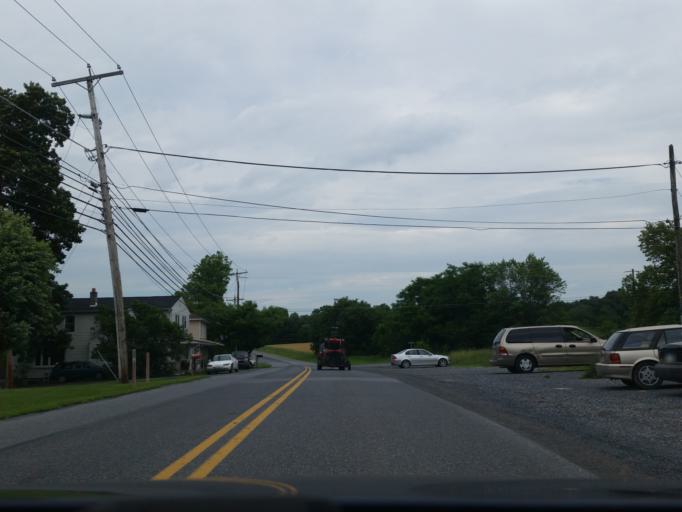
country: US
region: Pennsylvania
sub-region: Lebanon County
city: Jonestown
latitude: 40.4026
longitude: -76.5535
